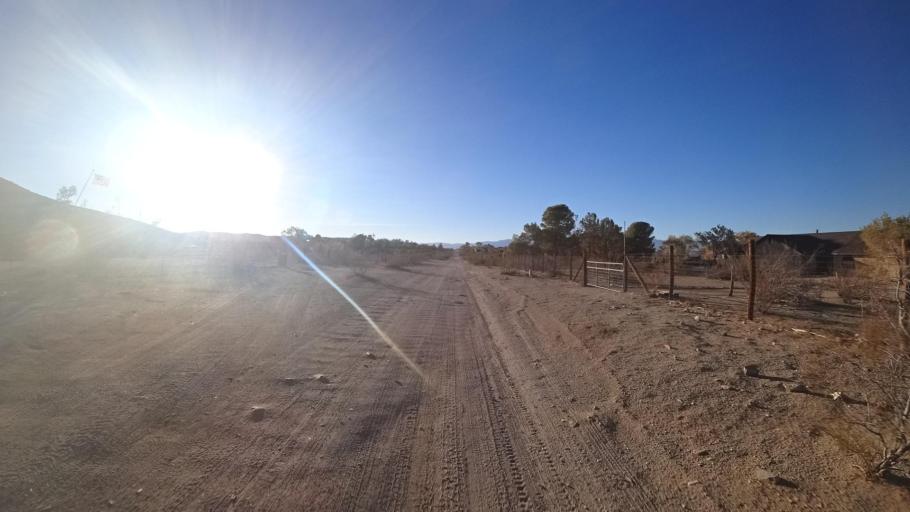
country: US
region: California
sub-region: Kern County
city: Ridgecrest
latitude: 35.5826
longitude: -117.6543
